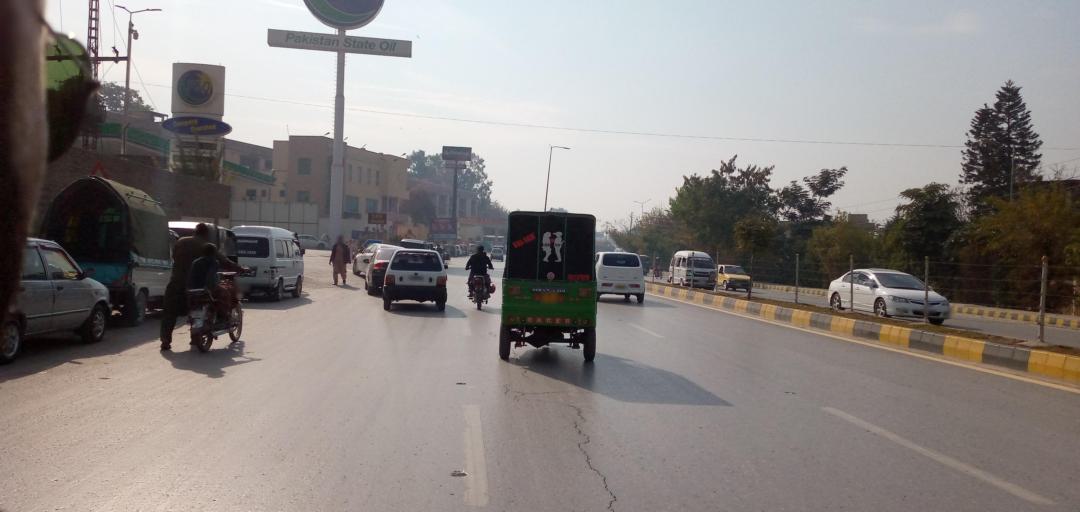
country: PK
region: Khyber Pakhtunkhwa
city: Peshawar
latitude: 34.0109
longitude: 71.5396
